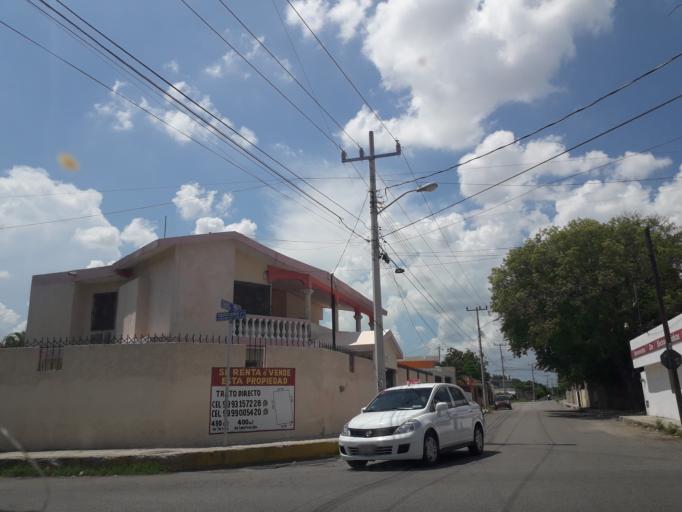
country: MX
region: Yucatan
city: Merida
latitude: 20.9646
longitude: -89.6482
